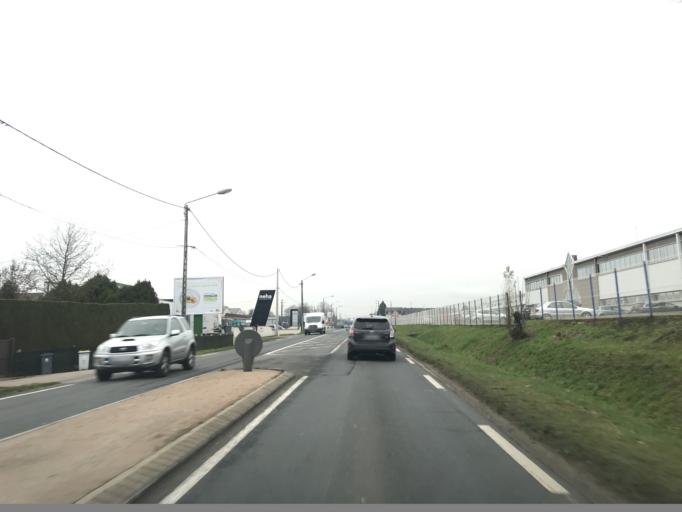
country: FR
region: Haute-Normandie
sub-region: Departement de la Seine-Maritime
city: Boos
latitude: 49.3965
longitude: 1.1813
